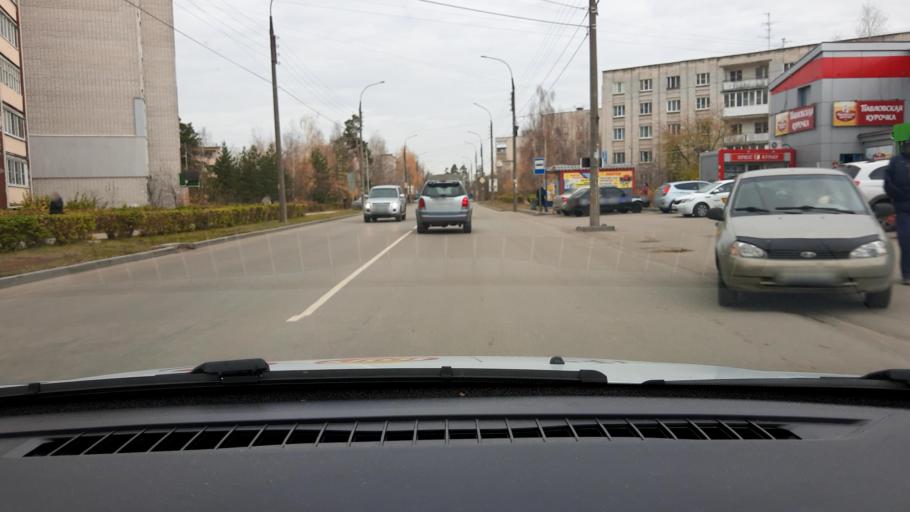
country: RU
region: Nizjnij Novgorod
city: Dzerzhinsk
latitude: 56.2535
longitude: 43.4507
